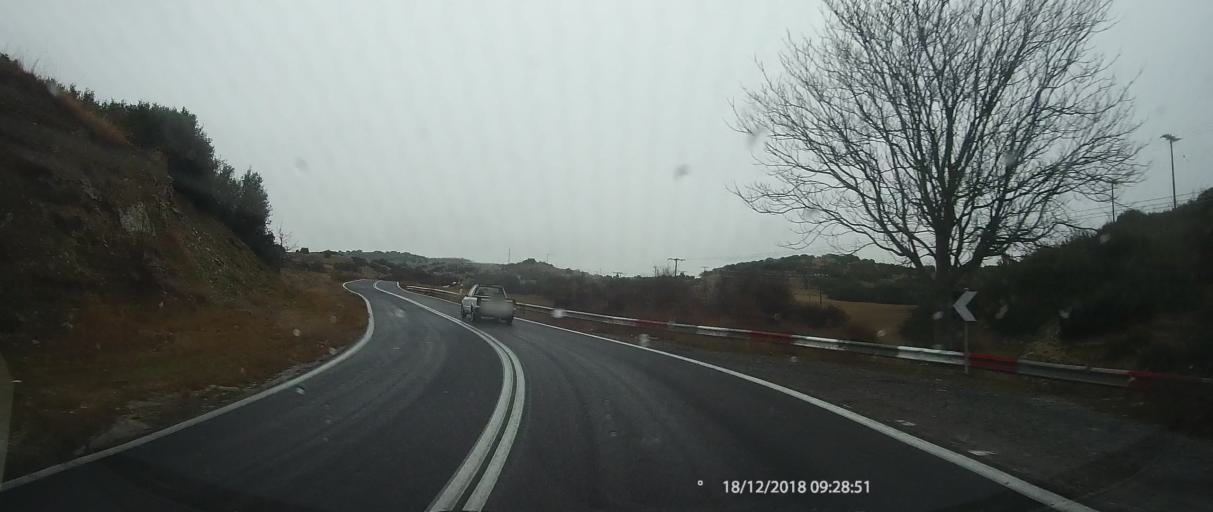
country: GR
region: Thessaly
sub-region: Nomos Larisis
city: Elassona
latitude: 39.9226
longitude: 22.1721
